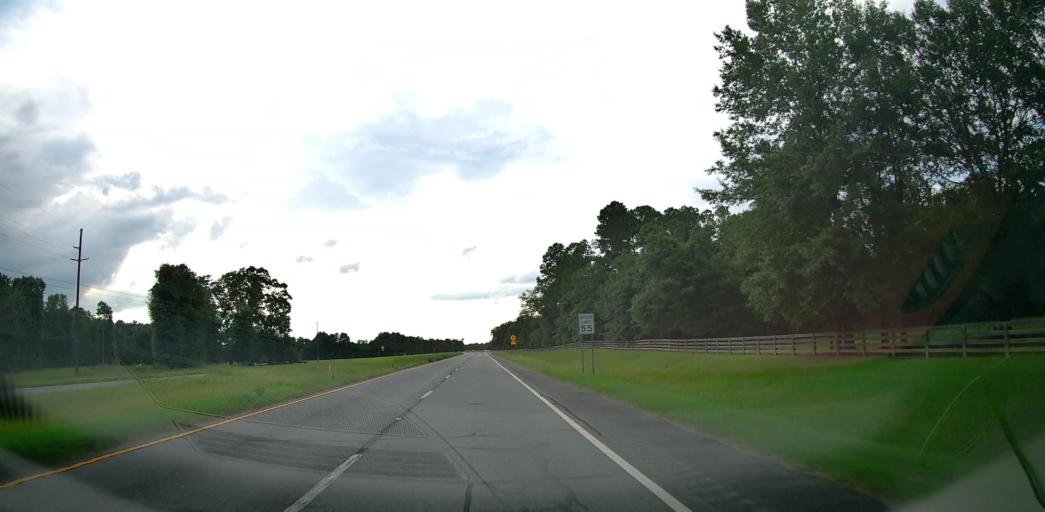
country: US
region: Georgia
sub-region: Pulaski County
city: Hawkinsville
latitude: 32.2720
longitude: -83.4183
